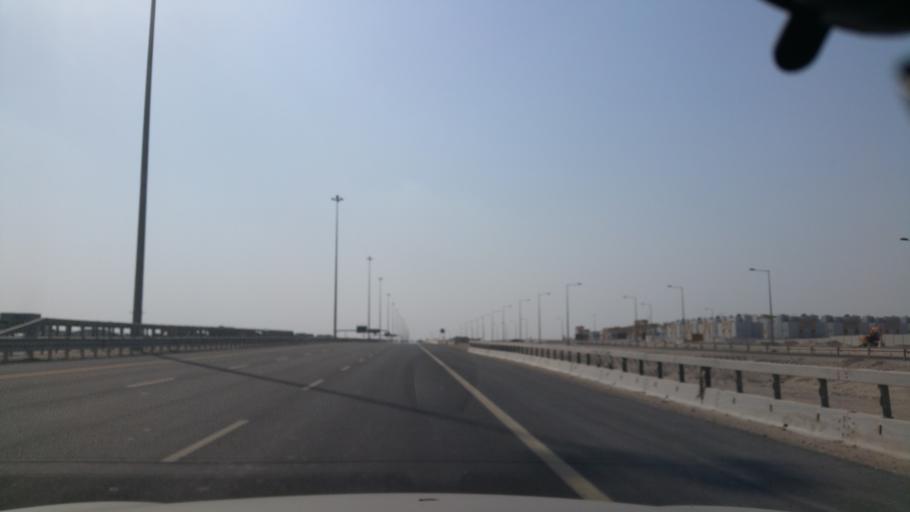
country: QA
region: Baladiyat Umm Salal
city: Umm Salal `Ali
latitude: 25.4569
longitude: 51.4705
